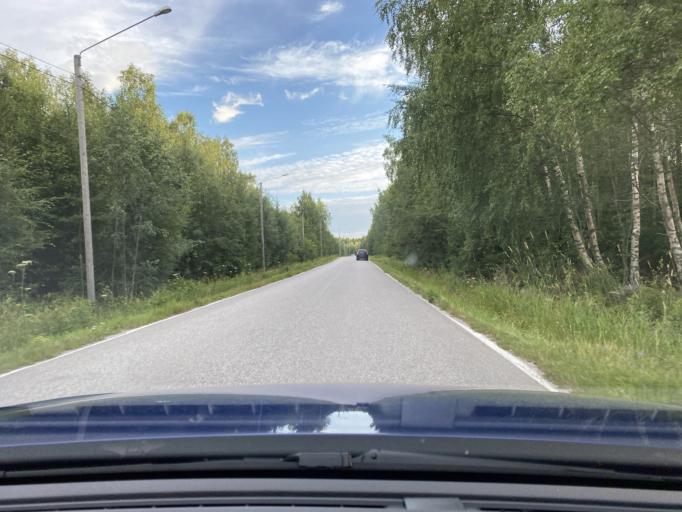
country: FI
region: Ostrobothnia
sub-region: Vaasa
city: Korsnaes
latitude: 62.9572
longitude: 21.1835
